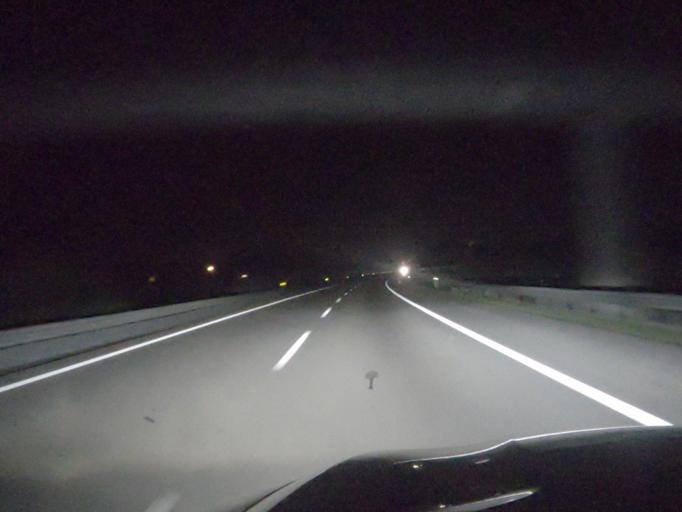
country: PT
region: Aveiro
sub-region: Anadia
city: Sangalhos
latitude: 40.4471
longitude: -8.5171
